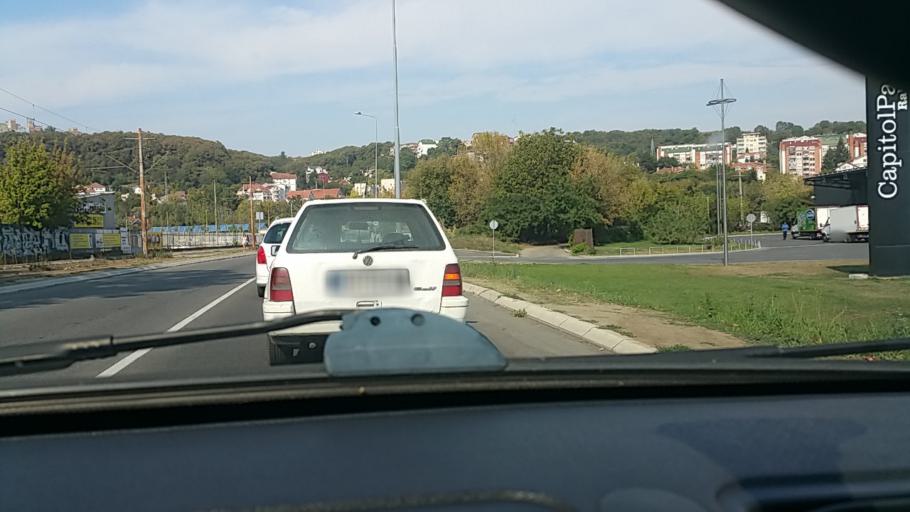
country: RS
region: Central Serbia
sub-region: Belgrade
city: Rakovica
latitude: 44.7389
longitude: 20.4366
